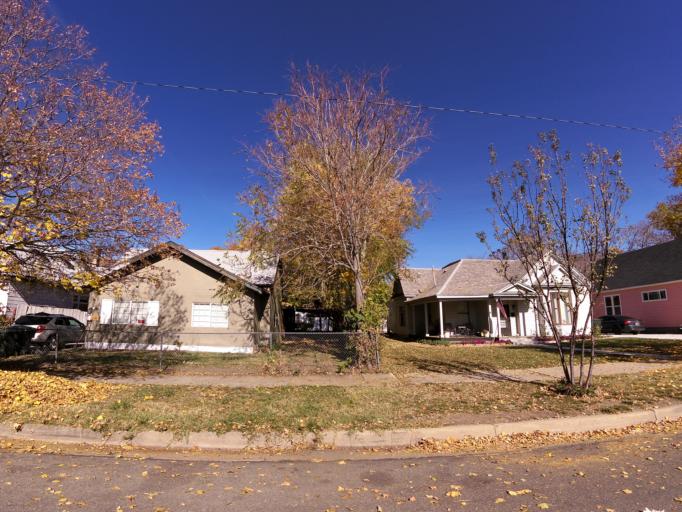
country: US
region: Utah
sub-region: Weber County
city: Ogden
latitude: 41.2247
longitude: -111.9602
